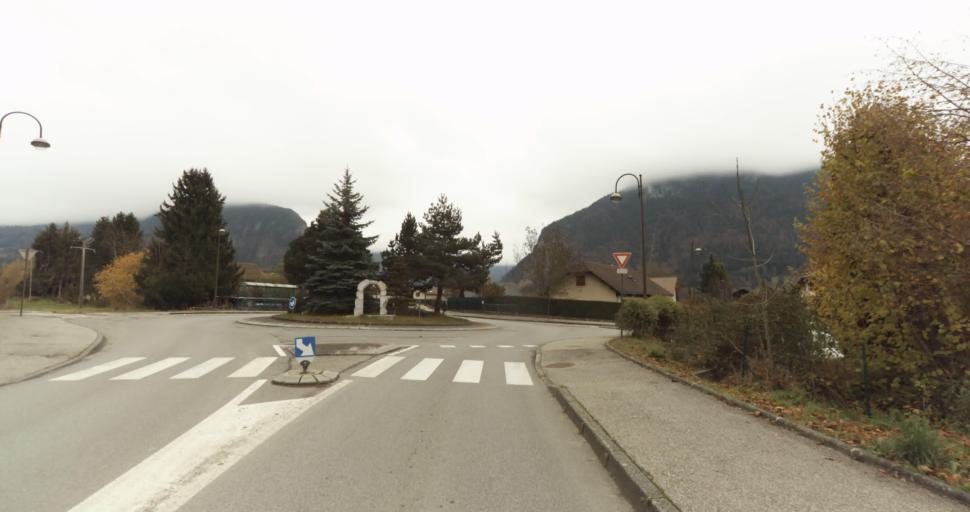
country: FR
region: Rhone-Alpes
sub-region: Departement de la Haute-Savoie
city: Thorens-Glieres
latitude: 45.9969
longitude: 6.2414
